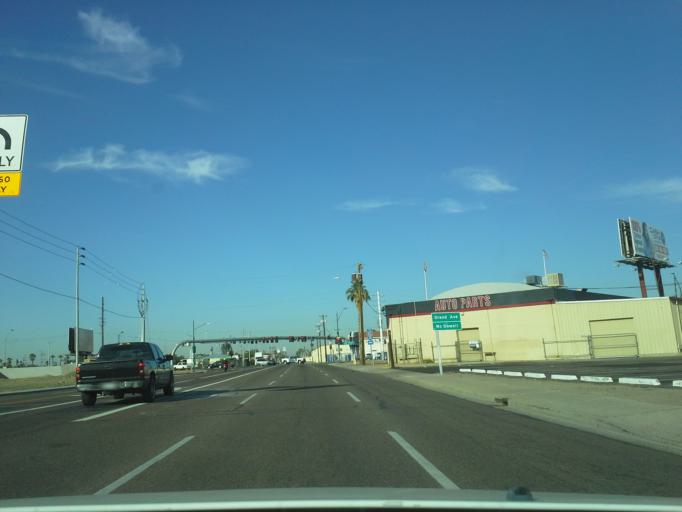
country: US
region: Arizona
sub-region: Maricopa County
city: Phoenix
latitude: 33.4644
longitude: -112.0999
